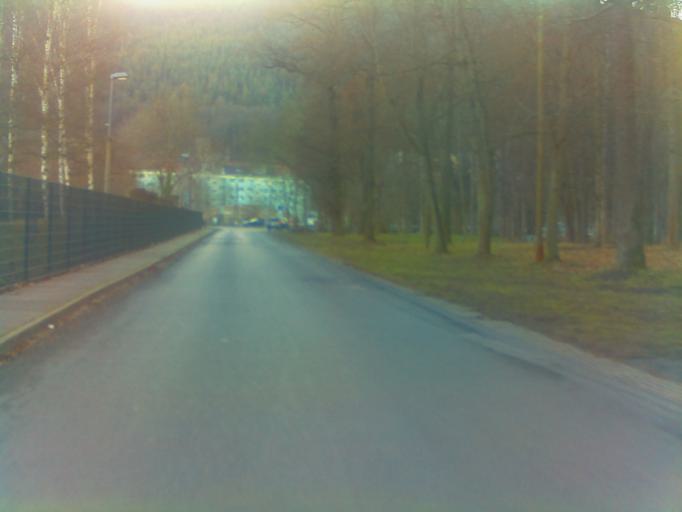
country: DE
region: Thuringia
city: Bad Blankenburg
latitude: 50.6778
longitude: 11.2727
